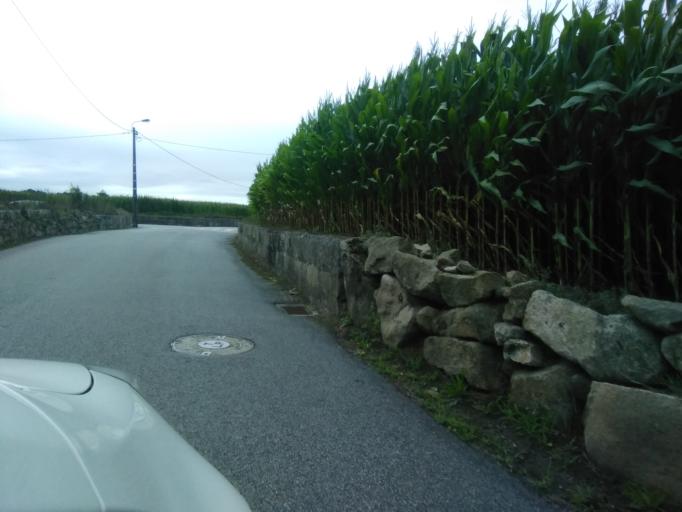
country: PT
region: Porto
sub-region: Matosinhos
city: Lavra
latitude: 41.2436
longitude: -8.7147
